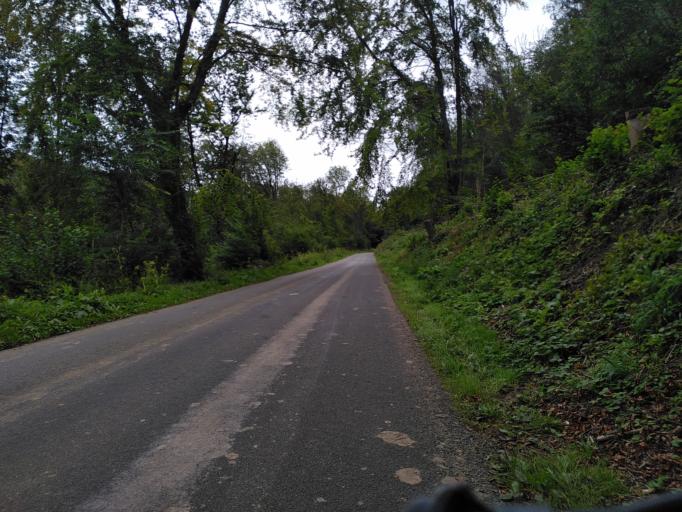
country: FR
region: Nord-Pas-de-Calais
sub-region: Departement du Pas-de-Calais
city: Desvres
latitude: 50.6651
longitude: 1.8654
